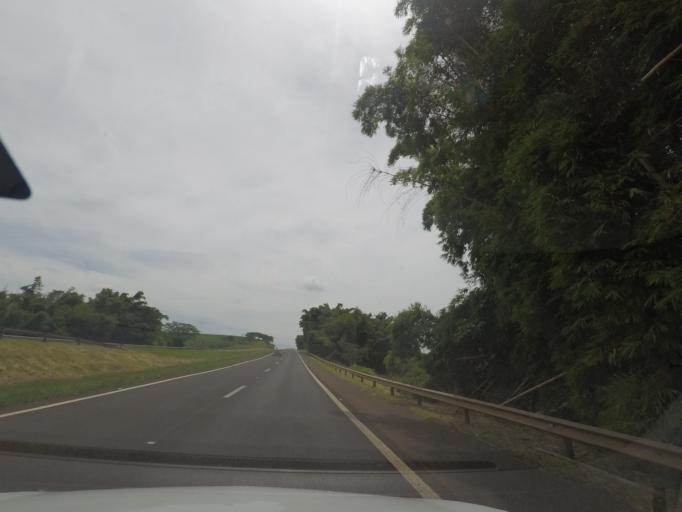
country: BR
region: Sao Paulo
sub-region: Bebedouro
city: Bebedouro
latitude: -21.0284
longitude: -48.4214
